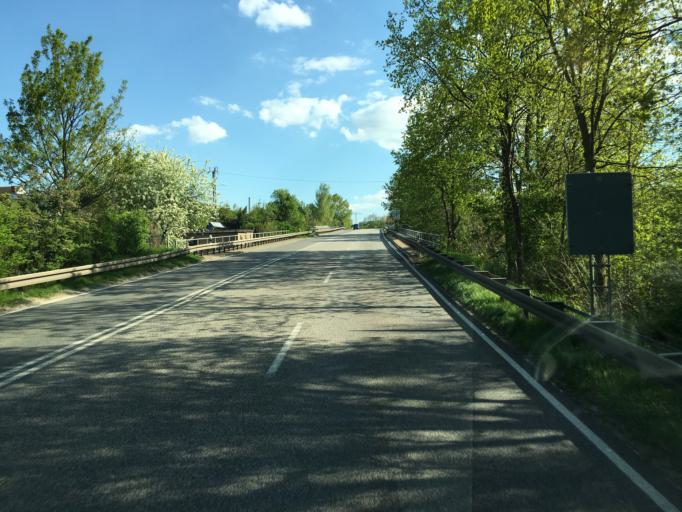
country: DE
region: Saxony
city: Dobeln
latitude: 51.1275
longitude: 13.0912
